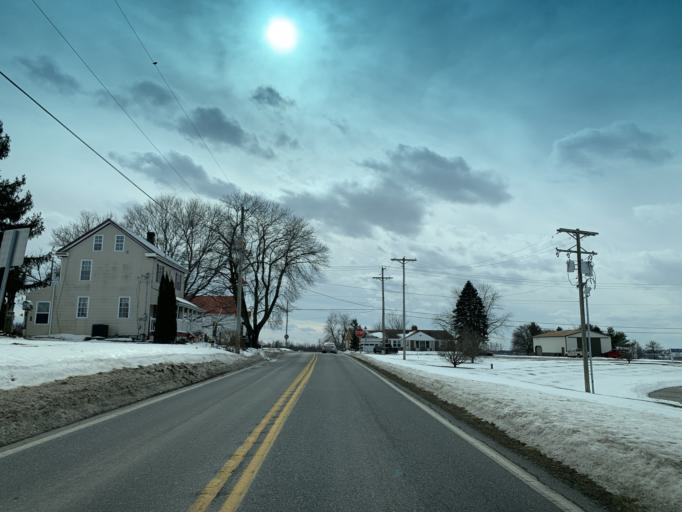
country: US
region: Pennsylvania
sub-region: York County
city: Shrewsbury
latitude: 39.7840
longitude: -76.6395
